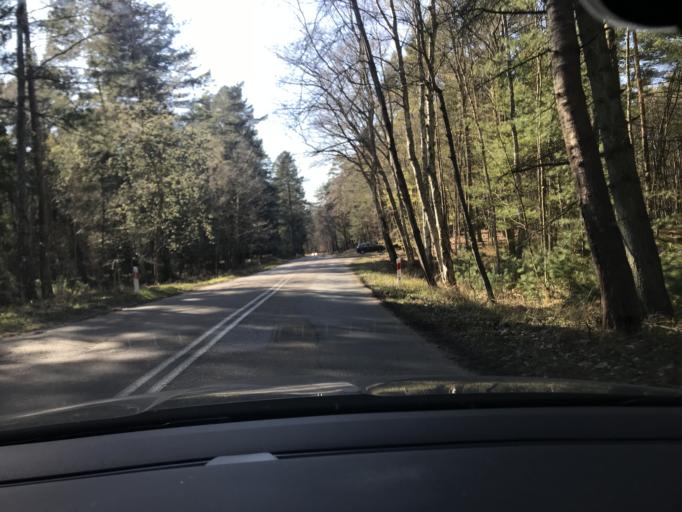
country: PL
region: Pomeranian Voivodeship
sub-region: Powiat nowodworski
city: Krynica Morska
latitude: 54.3562
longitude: 19.3256
